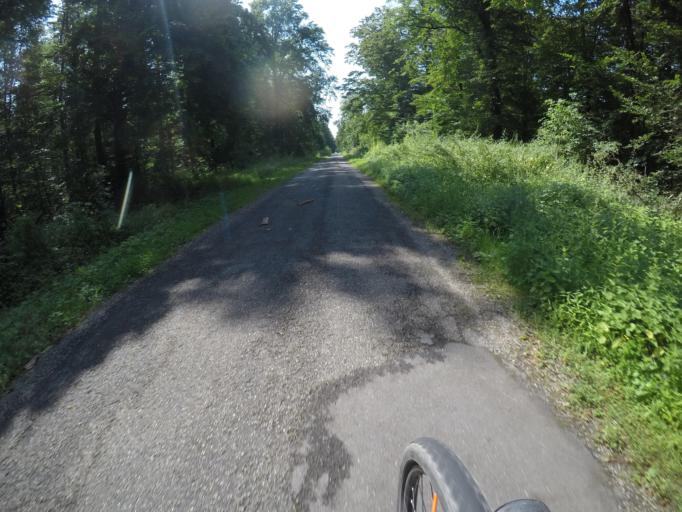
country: DE
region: Baden-Wuerttemberg
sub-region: Karlsruhe Region
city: Forst
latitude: 49.1805
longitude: 8.5969
